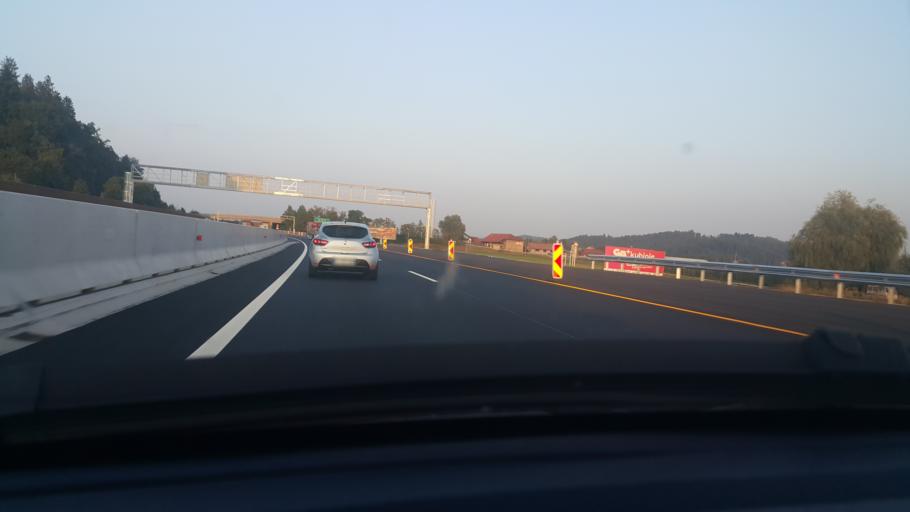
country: SI
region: Log-Dragomer
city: Log pri Brezovici
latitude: 46.0068
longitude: 14.3643
